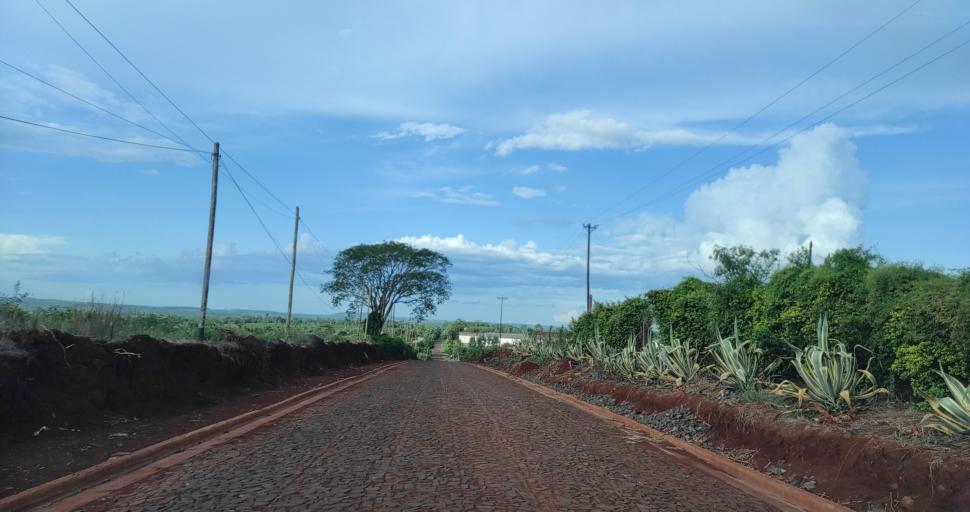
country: AR
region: Misiones
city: Santo Pipo
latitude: -27.1423
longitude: -55.4187
